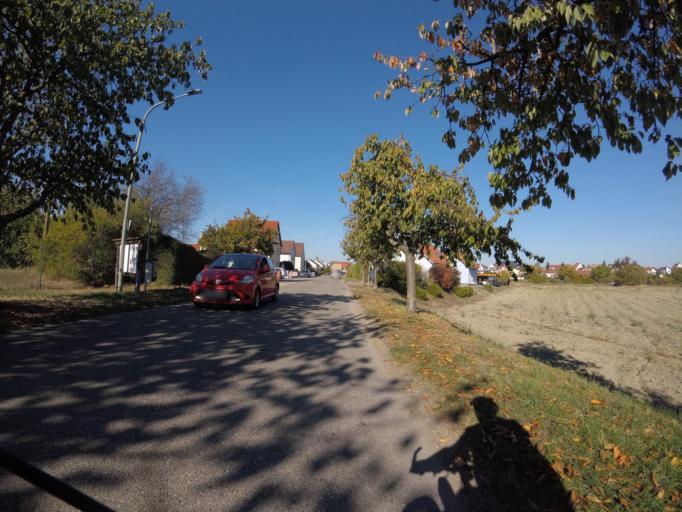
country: DE
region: Rheinland-Pfalz
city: Germersheim
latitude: 49.2621
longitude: 8.4038
